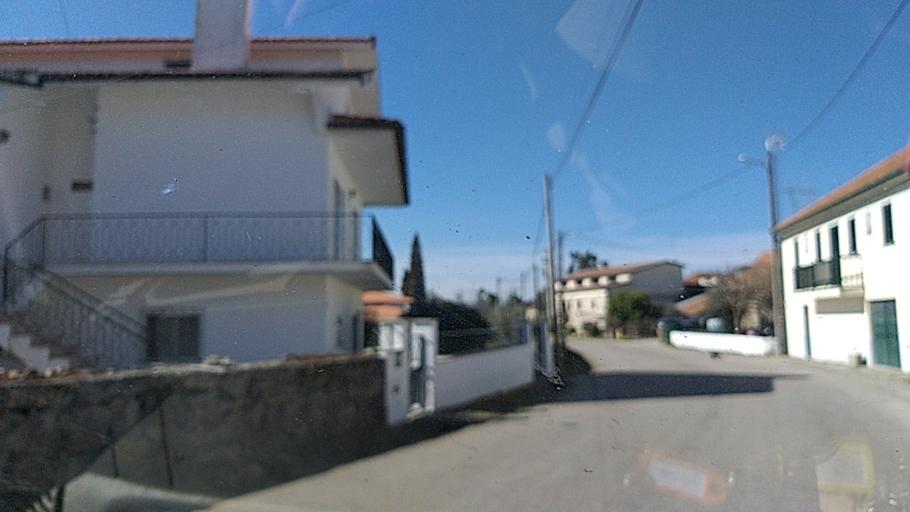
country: PT
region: Guarda
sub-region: Fornos de Algodres
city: Fornos de Algodres
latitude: 40.5950
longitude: -7.4689
